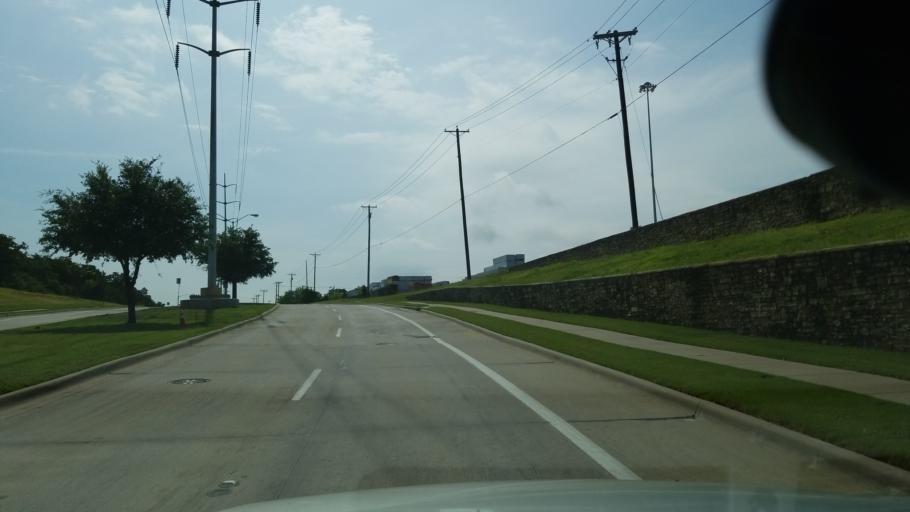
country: US
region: Texas
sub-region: Dallas County
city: Irving
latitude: 32.8441
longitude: -96.9338
